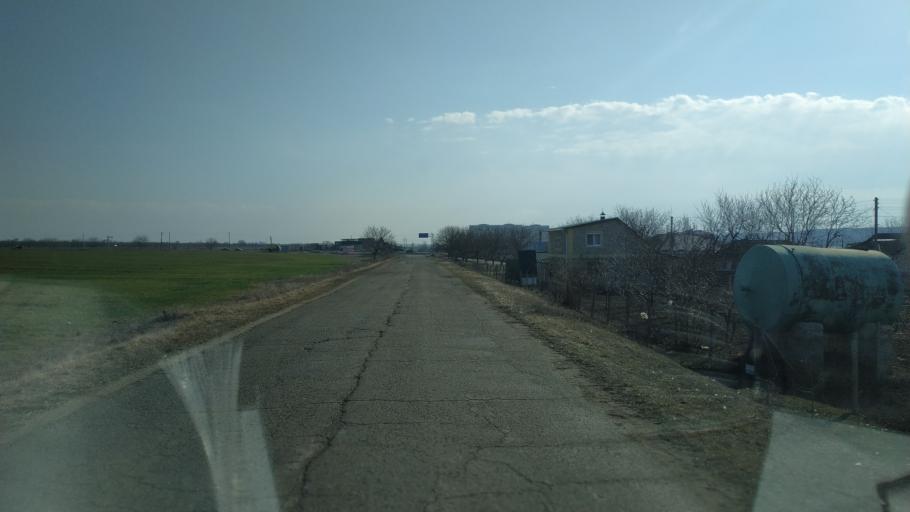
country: MD
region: Chisinau
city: Singera
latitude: 46.6881
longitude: 29.0482
